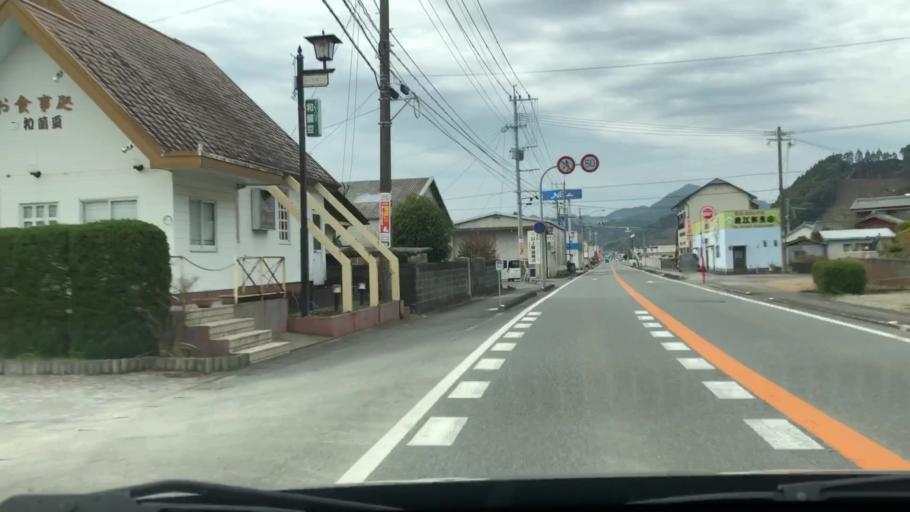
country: JP
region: Oita
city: Saiki
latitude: 32.9778
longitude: 131.8460
